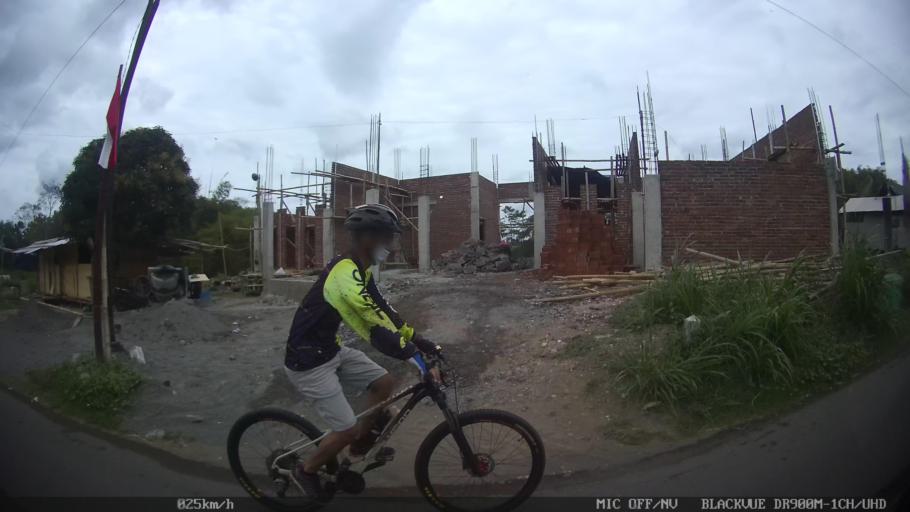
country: ID
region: Daerah Istimewa Yogyakarta
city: Sewon
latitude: -7.8635
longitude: 110.4212
